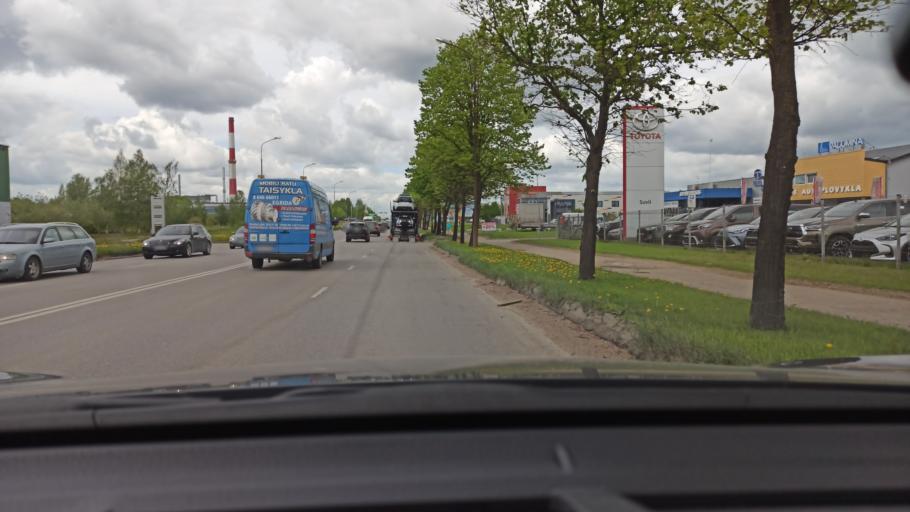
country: LT
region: Siauliu apskritis
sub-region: Siauliai
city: Siauliai
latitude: 55.9072
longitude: 23.3233
